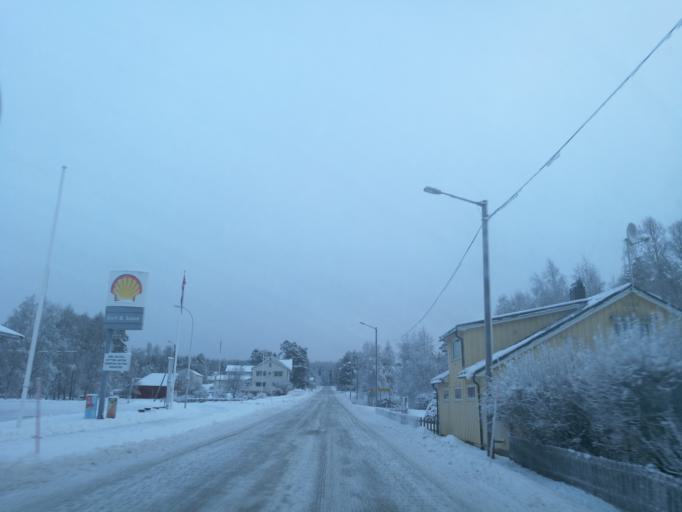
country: NO
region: Hedmark
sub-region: Grue
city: Kirkenaer
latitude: 60.4174
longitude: 12.4015
